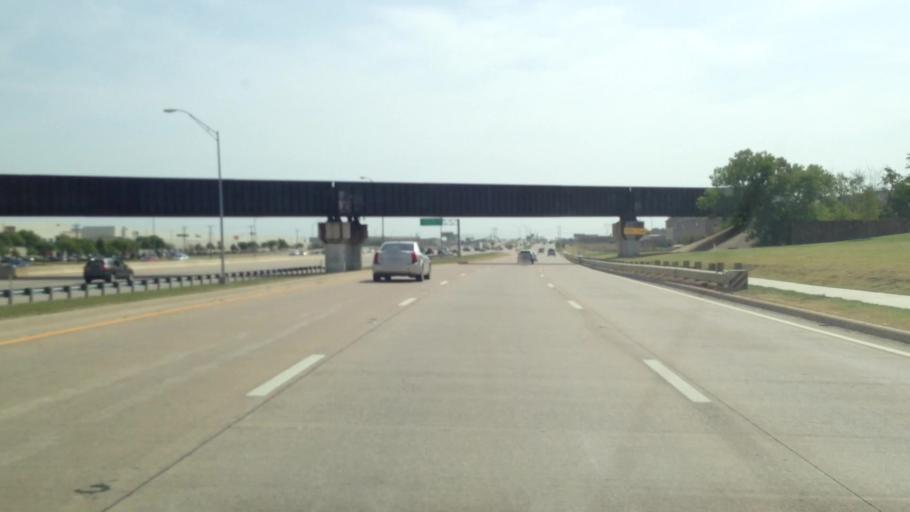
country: US
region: Texas
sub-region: Denton County
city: The Colony
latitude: 33.0532
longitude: -96.9155
